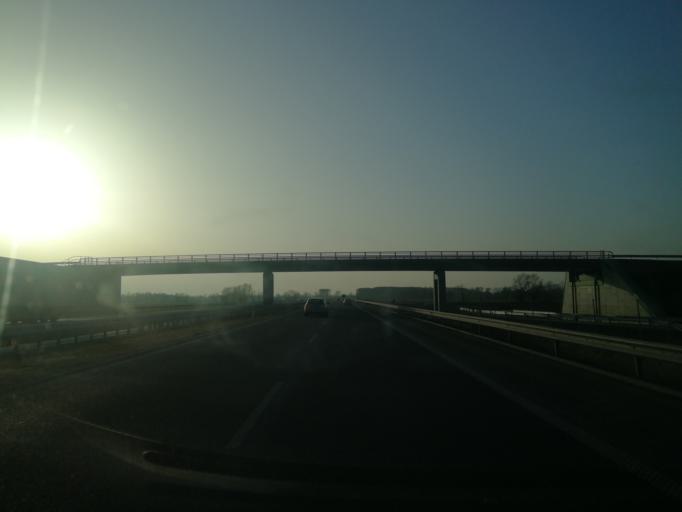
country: PL
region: Warmian-Masurian Voivodeship
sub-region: Powiat elblaski
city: Gronowo Elblaskie
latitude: 54.1645
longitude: 19.2705
